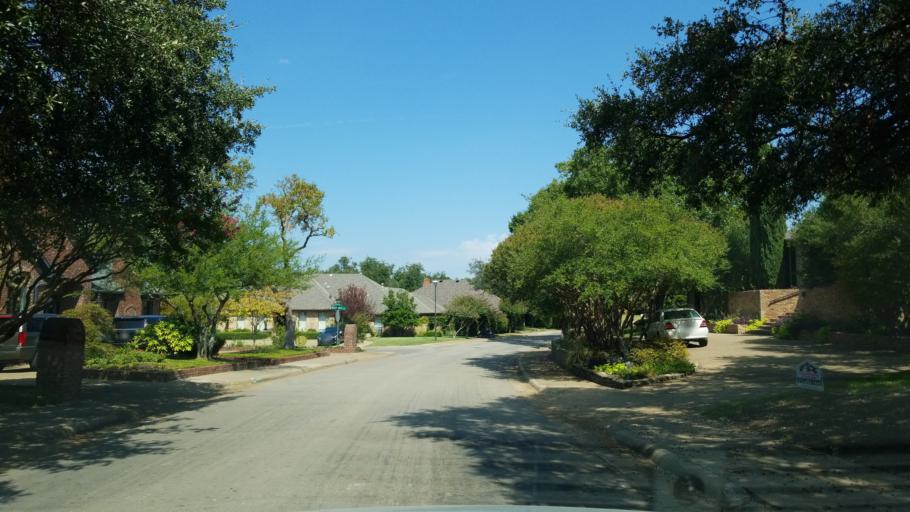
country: US
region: Texas
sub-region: Dallas County
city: Addison
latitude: 32.9669
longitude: -96.8009
